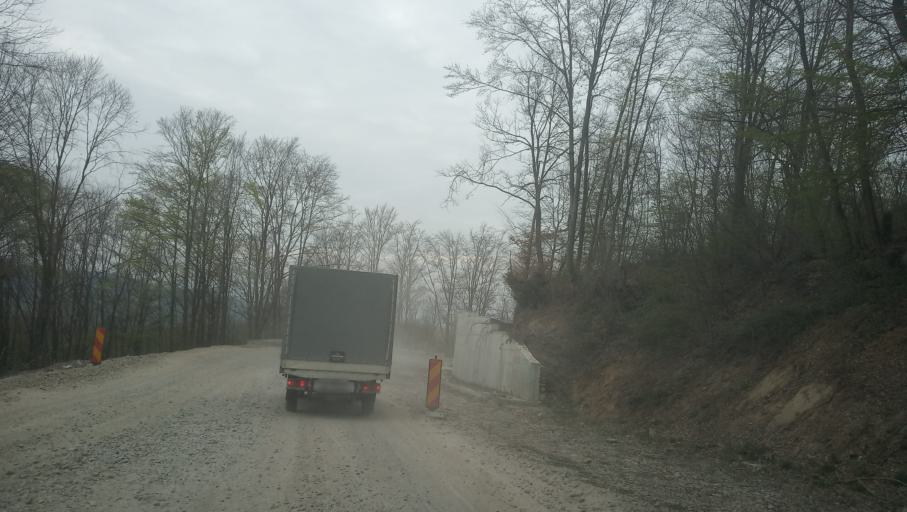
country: RO
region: Arad
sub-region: Comuna Varfurile
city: Varfurile
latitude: 46.3698
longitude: 22.5541
